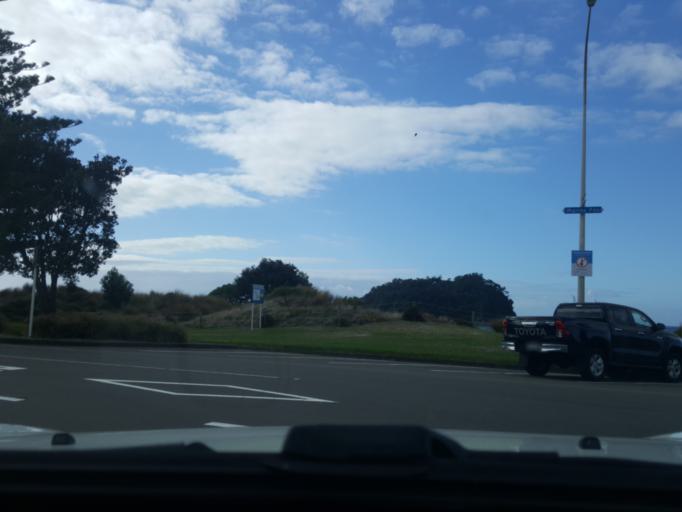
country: NZ
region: Bay of Plenty
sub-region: Tauranga City
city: Tauranga
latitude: -37.6370
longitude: 176.1877
